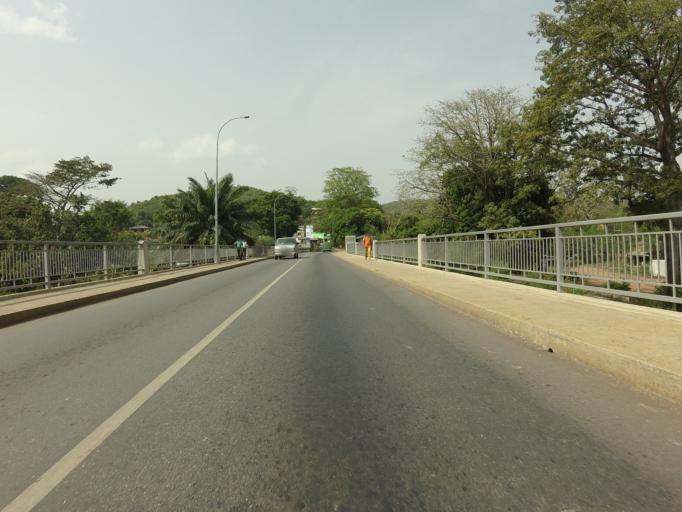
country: GH
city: Akropong
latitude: 6.2396
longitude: 0.0943
